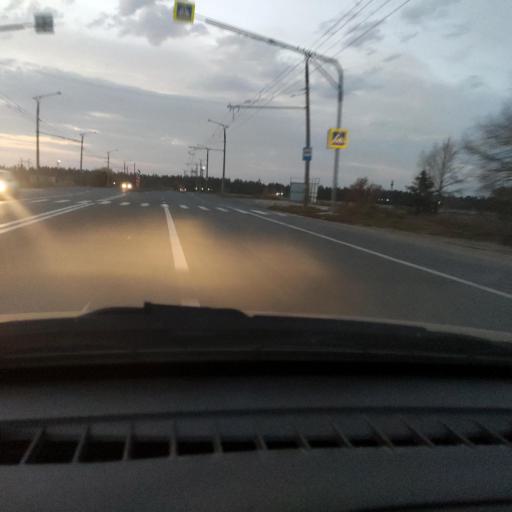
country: RU
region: Samara
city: Povolzhskiy
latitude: 53.5460
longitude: 49.6038
